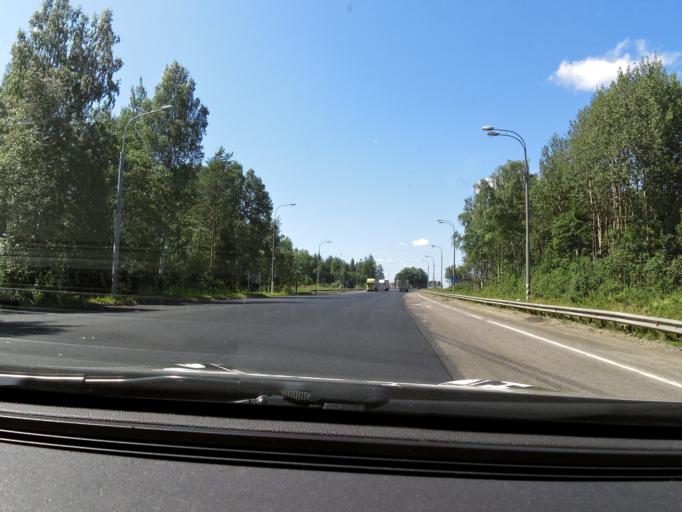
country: RU
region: Novgorod
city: Valday
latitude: 57.9554
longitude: 33.2545
